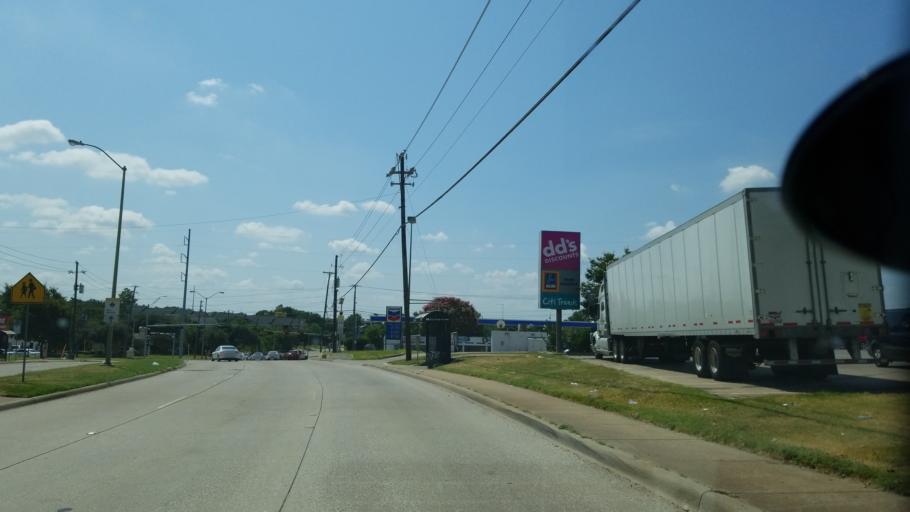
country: US
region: Texas
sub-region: Dallas County
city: Richardson
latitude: 32.9108
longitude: -96.7183
